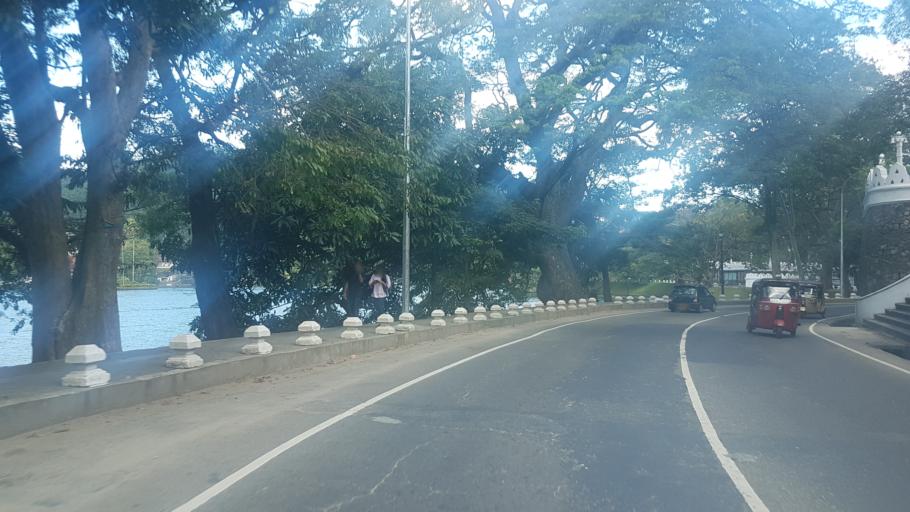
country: LK
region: Central
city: Kandy
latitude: 7.2902
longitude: 80.6388
